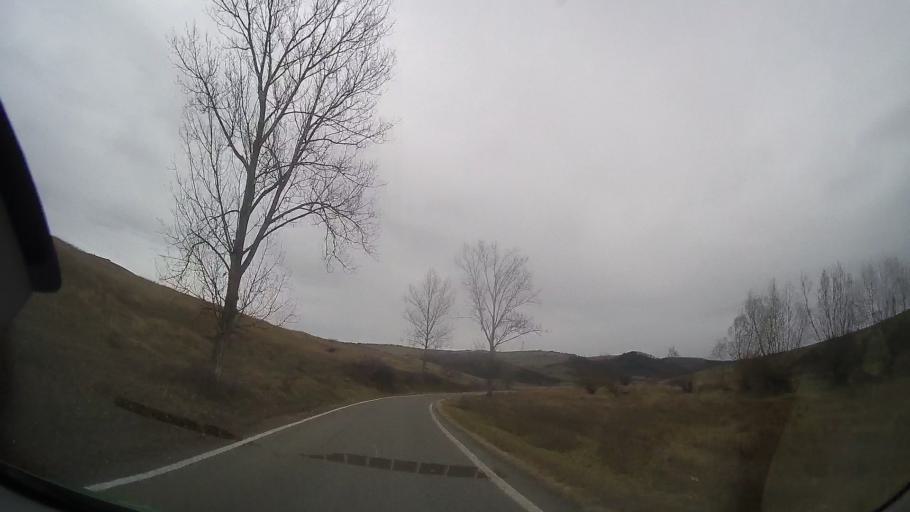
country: RO
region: Mures
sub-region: Comuna Bala
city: Bala
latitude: 46.7165
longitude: 24.5477
